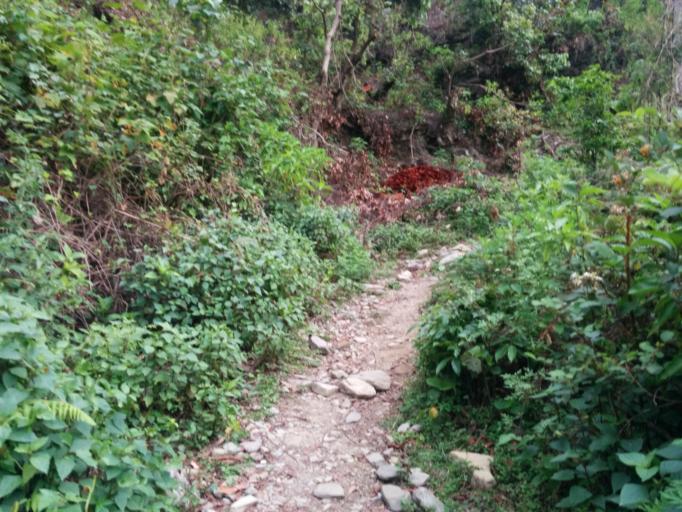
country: NP
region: Western Region
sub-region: Gandaki Zone
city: Pokhara
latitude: 28.2321
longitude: 83.9500
